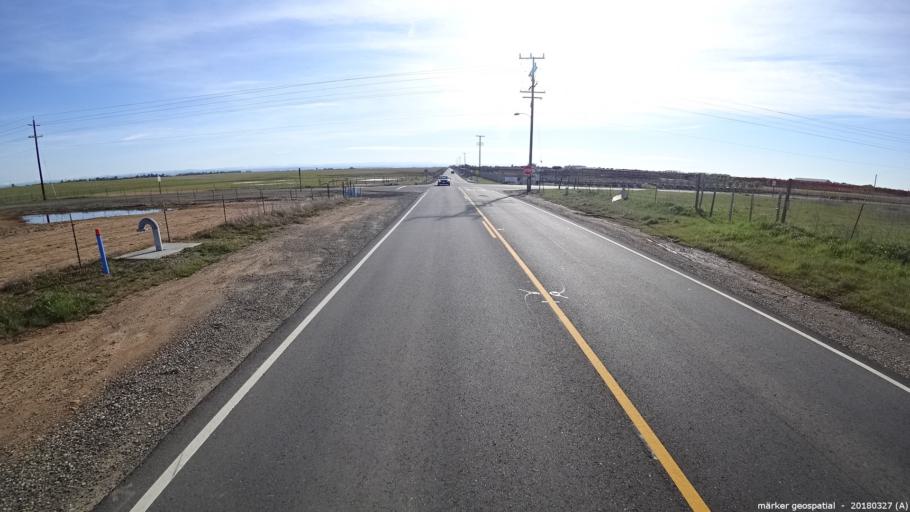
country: US
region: California
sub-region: Sacramento County
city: Vineyard
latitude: 38.4963
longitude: -121.2984
